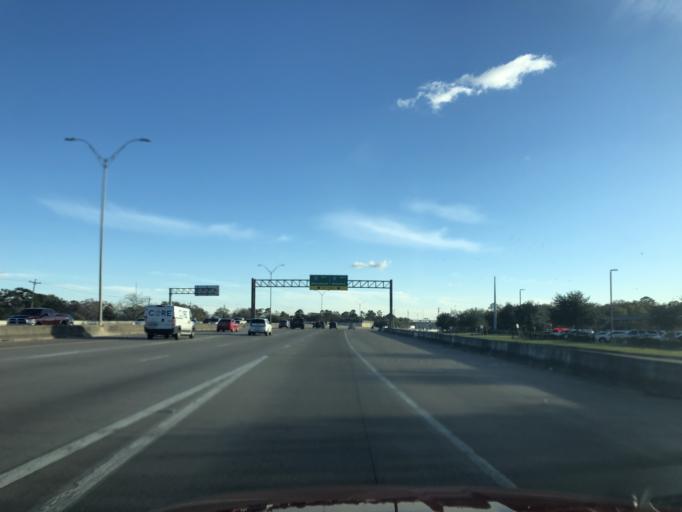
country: US
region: Texas
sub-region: Harris County
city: Cloverleaf
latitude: 29.7864
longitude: -95.1597
